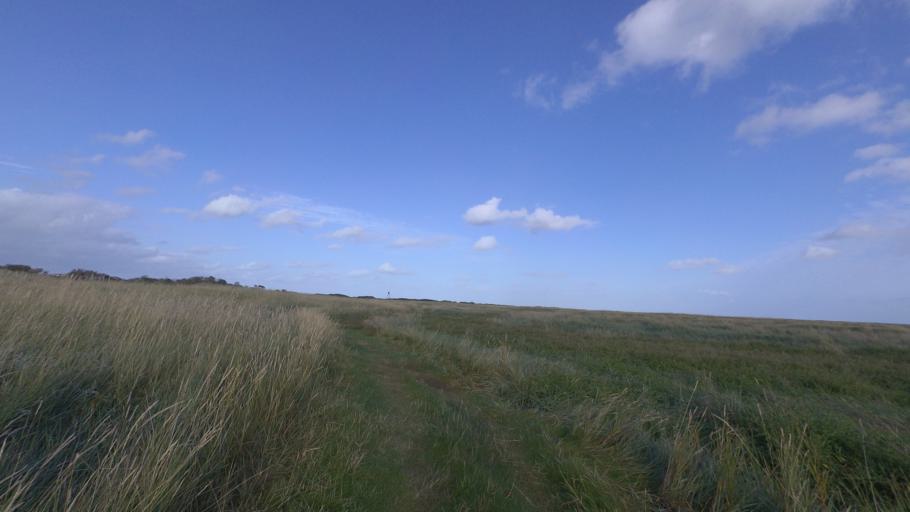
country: NL
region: Friesland
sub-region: Gemeente Dongeradeel
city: Ternaard
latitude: 53.4593
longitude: 5.9187
